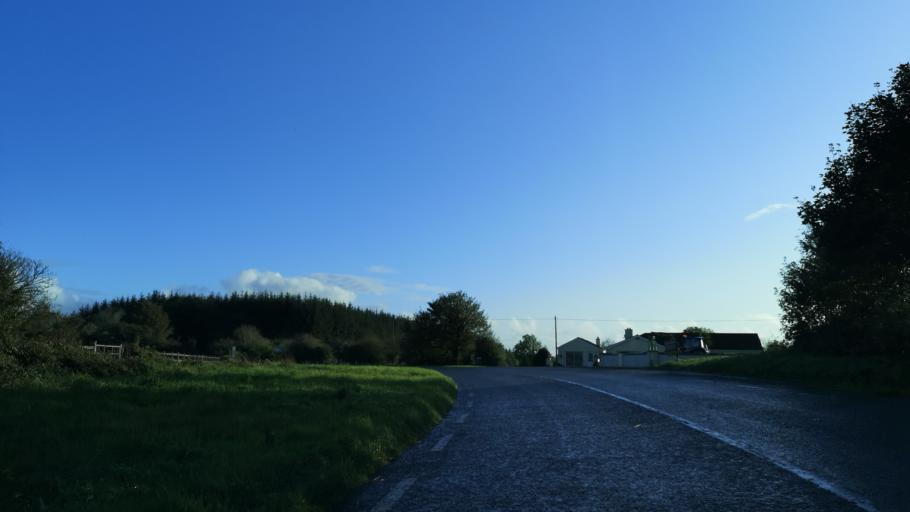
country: IE
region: Connaught
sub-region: Roscommon
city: Castlerea
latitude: 53.7877
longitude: -8.4913
